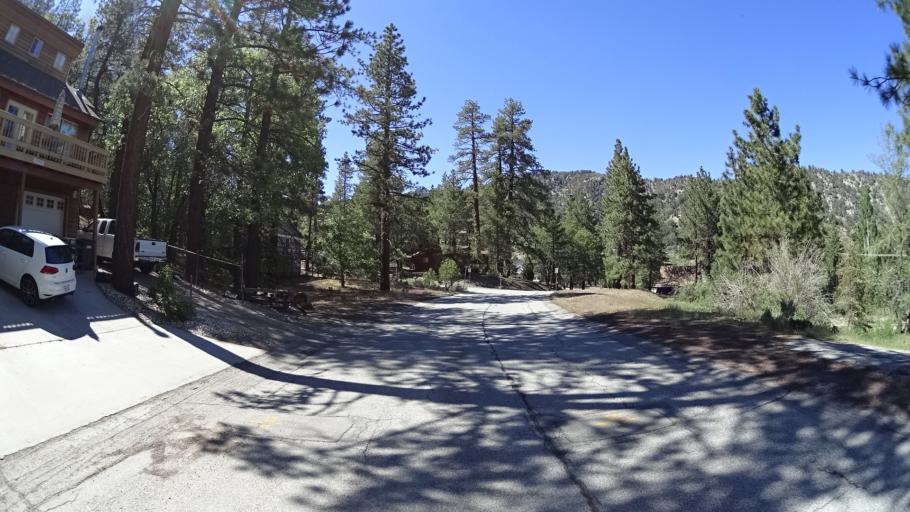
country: US
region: California
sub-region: San Bernardino County
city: Wrightwood
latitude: 34.3643
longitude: -117.6537
